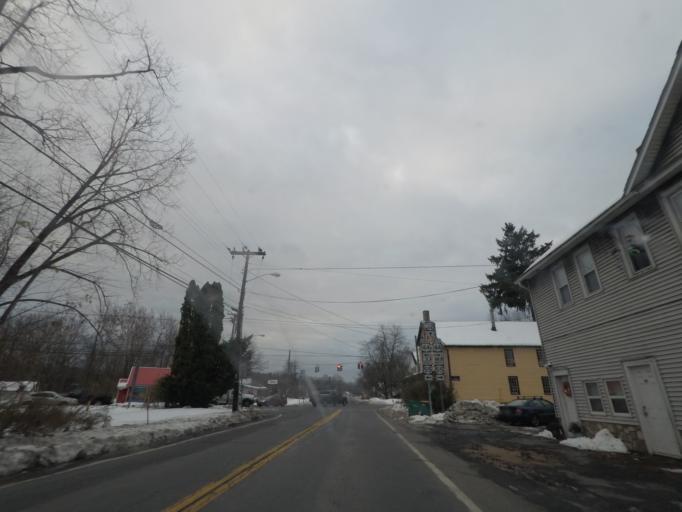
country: US
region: New York
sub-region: Ulster County
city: Plattekill
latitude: 41.6685
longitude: -74.1060
